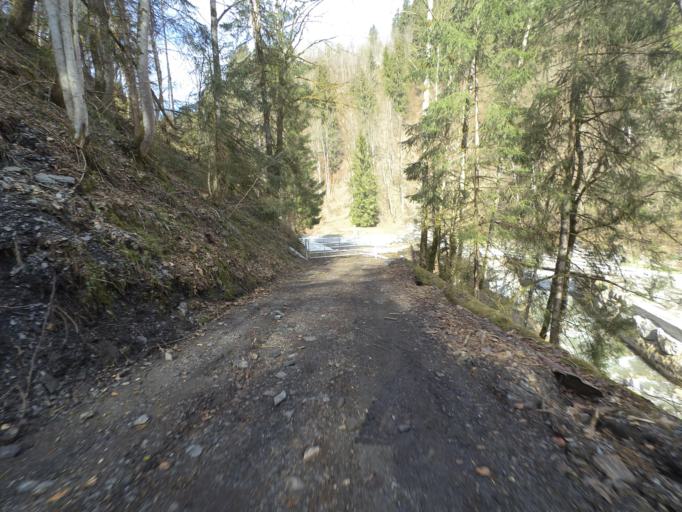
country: AT
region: Salzburg
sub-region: Politischer Bezirk Sankt Johann im Pongau
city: Sankt Veit im Pongau
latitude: 47.3290
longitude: 13.1327
